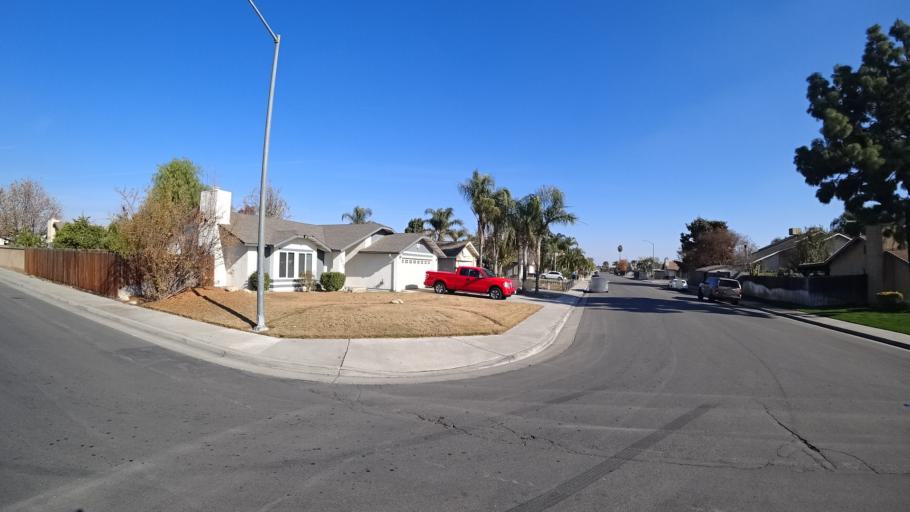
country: US
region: California
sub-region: Kern County
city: Greenfield
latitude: 35.3017
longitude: -119.0430
